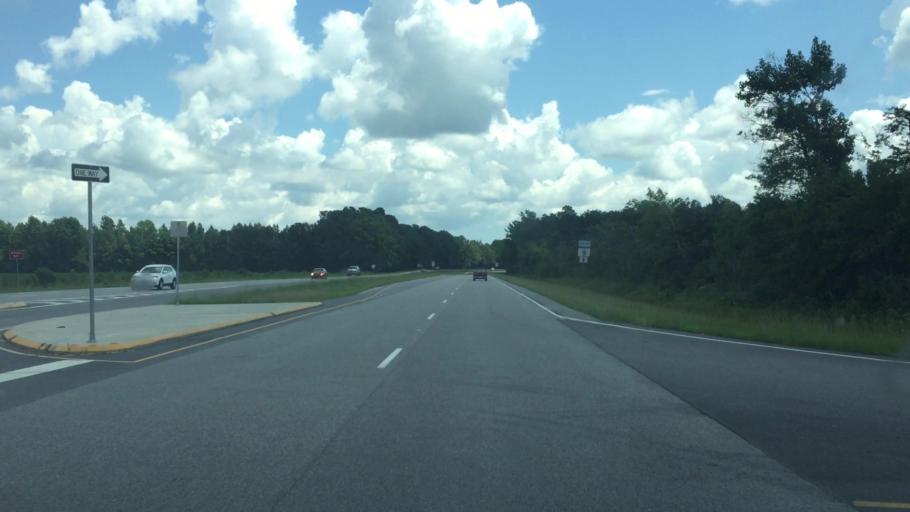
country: US
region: South Carolina
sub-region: Horry County
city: Loris
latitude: 34.0344
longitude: -78.8094
